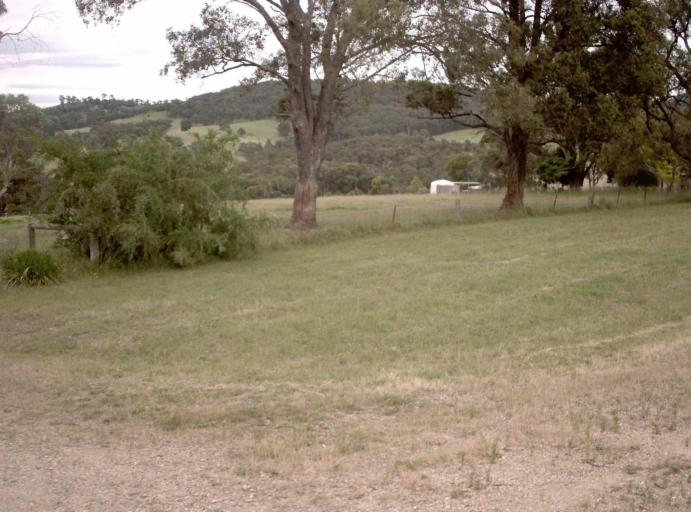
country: AU
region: Victoria
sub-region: East Gippsland
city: Bairnsdale
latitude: -37.7354
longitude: 147.5945
